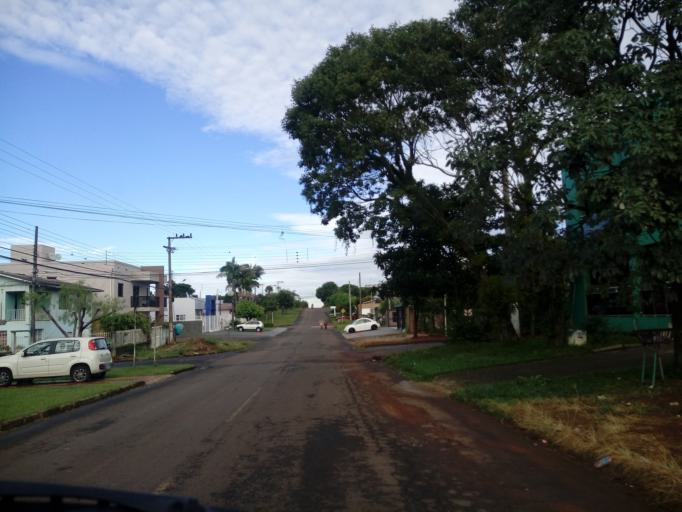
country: BR
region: Santa Catarina
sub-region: Chapeco
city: Chapeco
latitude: -27.1085
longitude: -52.6312
